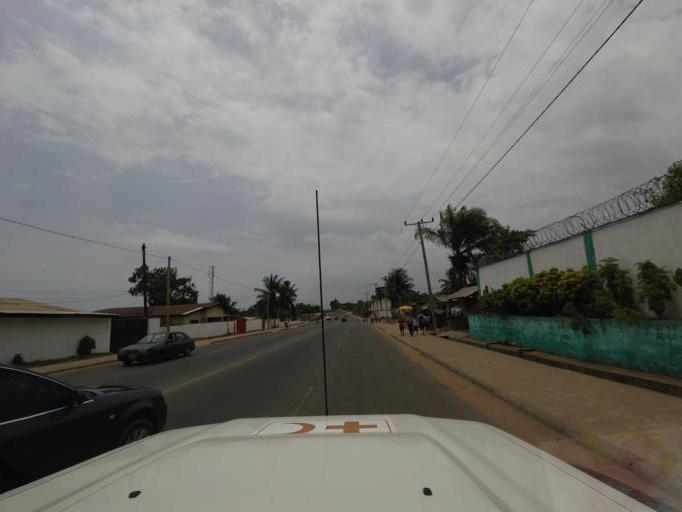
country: LR
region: Montserrado
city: Monrovia
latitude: 6.2743
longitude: -10.7135
